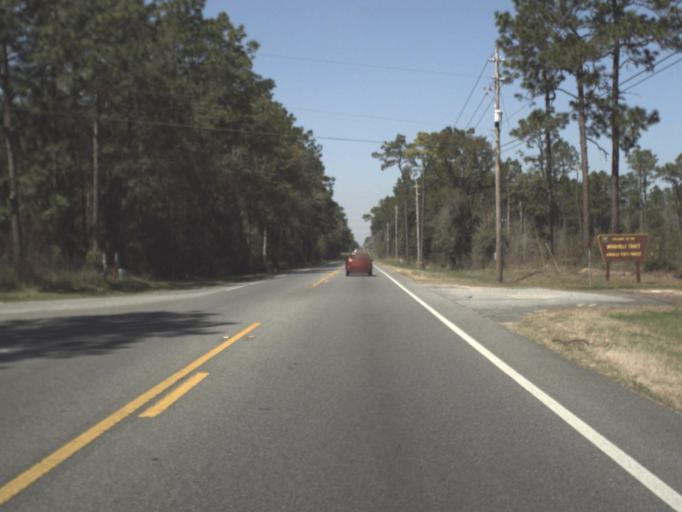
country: US
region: Florida
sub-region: Leon County
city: Woodville
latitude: 30.3420
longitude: -84.2554
